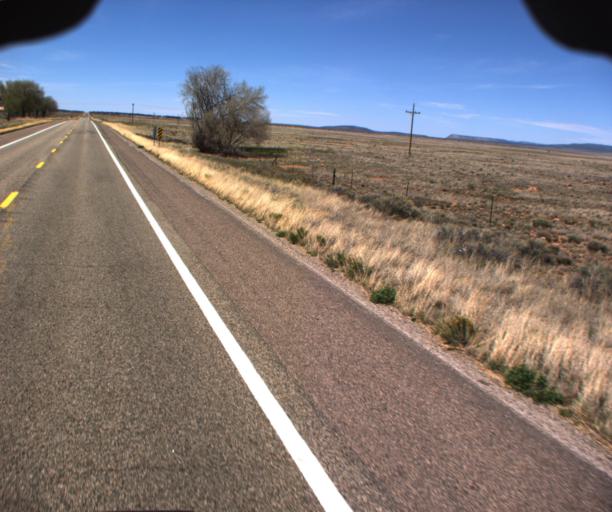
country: US
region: Arizona
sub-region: Mohave County
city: Peach Springs
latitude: 35.4767
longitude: -113.1351
